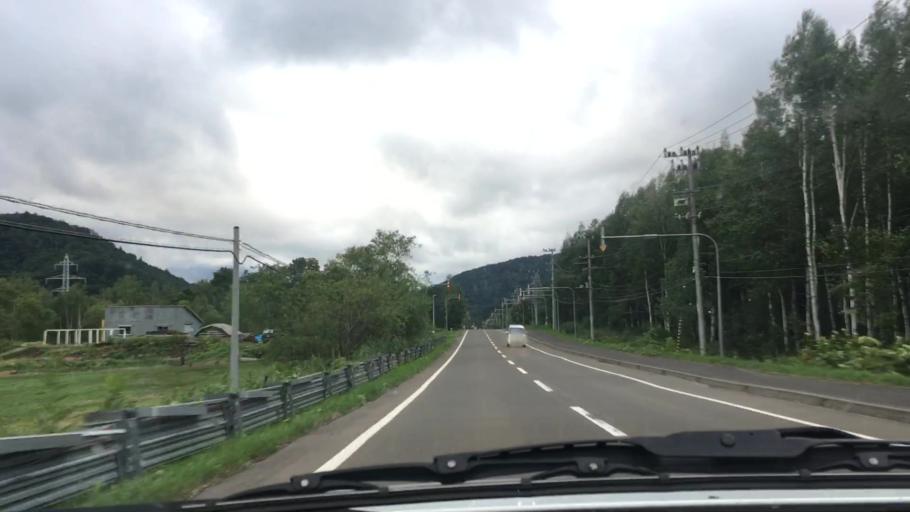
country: JP
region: Hokkaido
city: Shimo-furano
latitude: 43.0555
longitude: 142.6272
